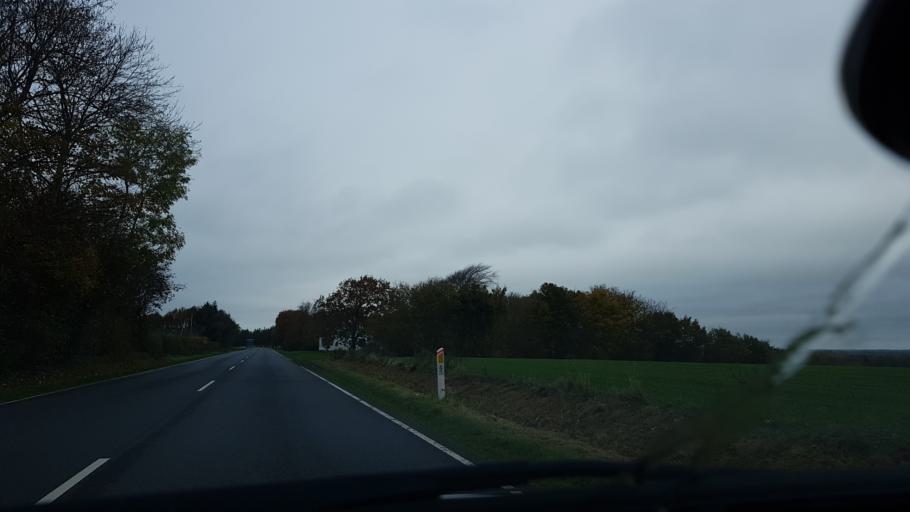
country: DK
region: South Denmark
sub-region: Esbjerg Kommune
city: Ribe
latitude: 55.2769
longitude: 8.8619
